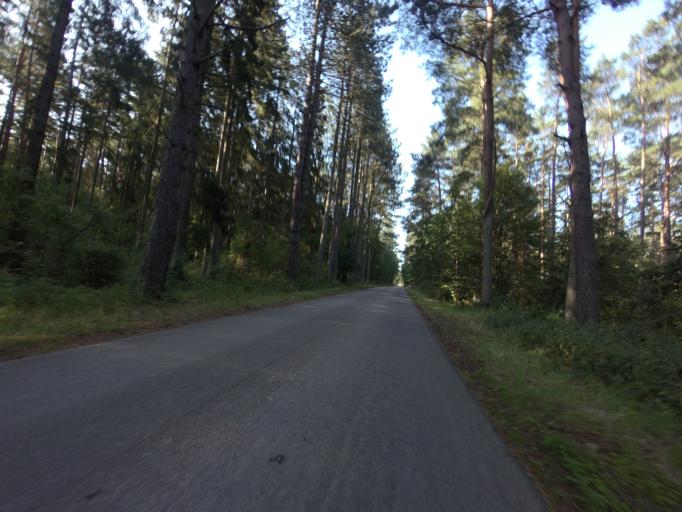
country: SE
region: Skane
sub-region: Landskrona
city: Asmundtorp
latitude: 55.8406
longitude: 12.9326
